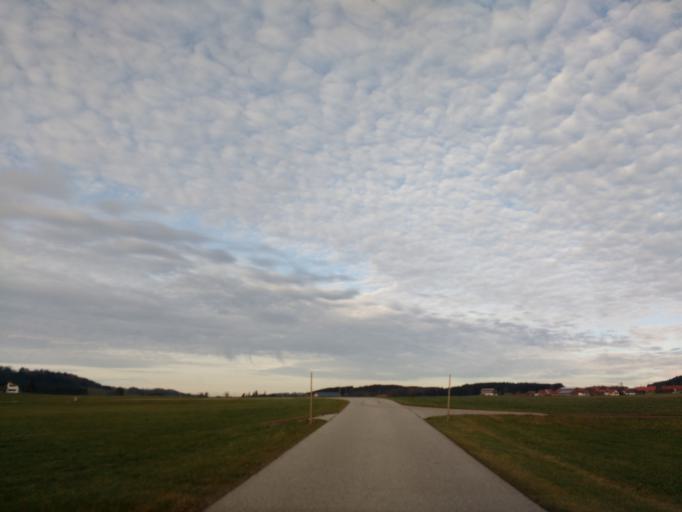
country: DE
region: Bavaria
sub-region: Swabia
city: Wildpoldsried
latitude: 47.7948
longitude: 10.4100
